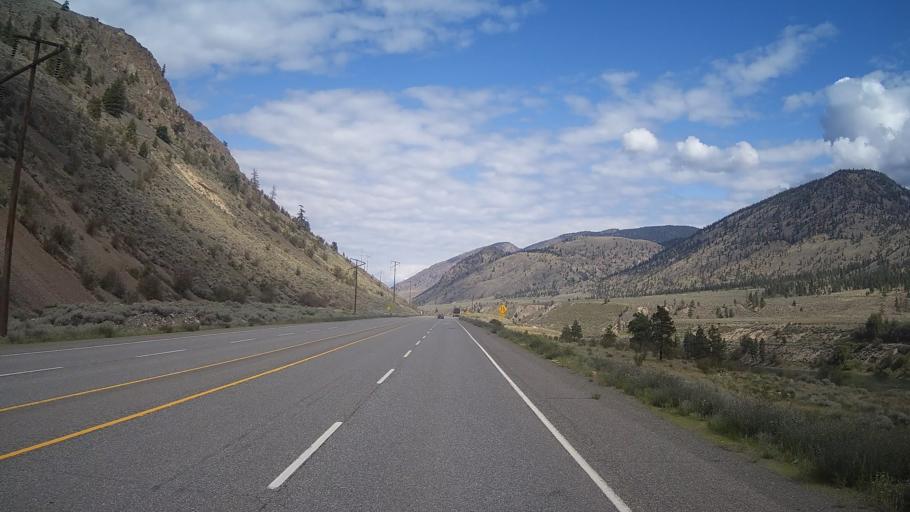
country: CA
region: British Columbia
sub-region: Thompson-Nicola Regional District
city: Ashcroft
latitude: 50.5252
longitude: -121.2856
